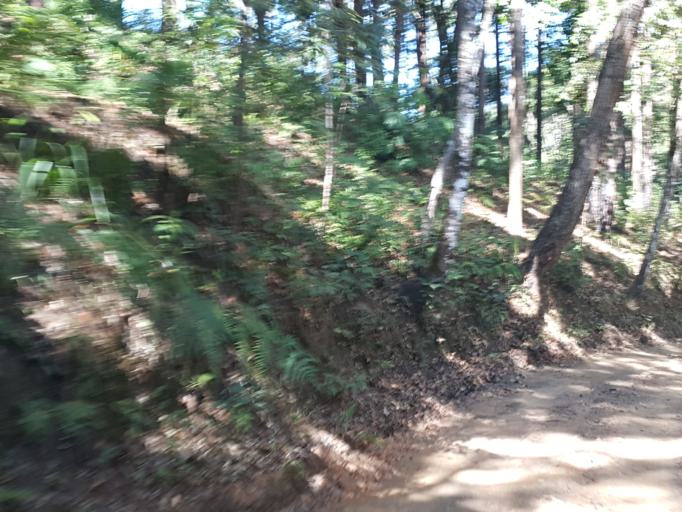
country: TH
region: Chiang Mai
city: Wiang Haeng
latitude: 19.5253
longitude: 98.8096
